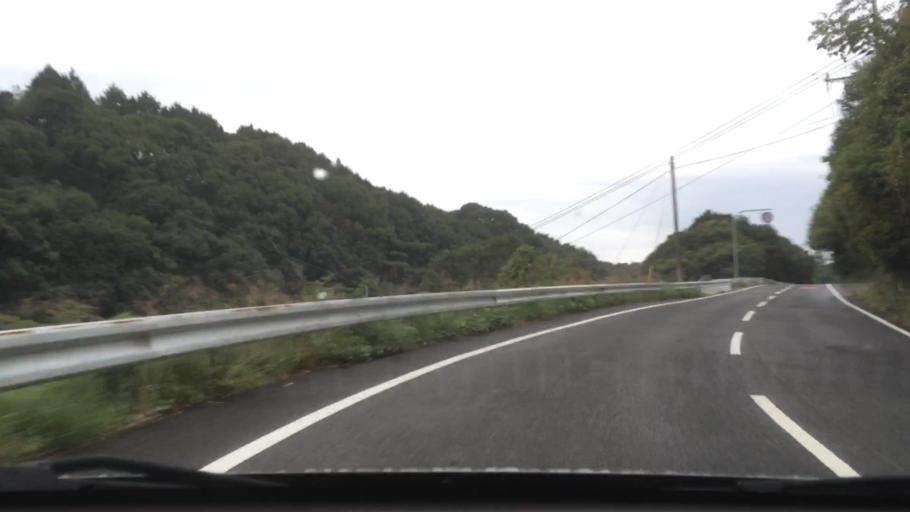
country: JP
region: Nagasaki
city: Sasebo
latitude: 32.9591
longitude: 129.6806
